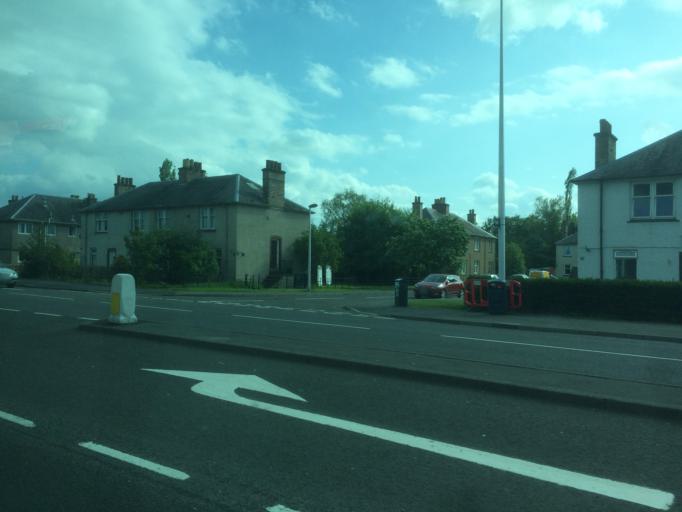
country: GB
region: Scotland
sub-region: Perth and Kinross
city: Perth
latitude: 56.4076
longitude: -3.4483
